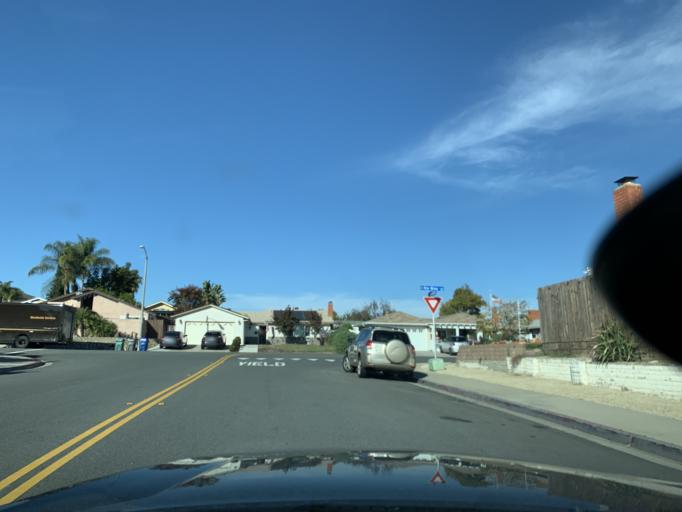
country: US
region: California
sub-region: San Diego County
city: Santee
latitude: 32.8553
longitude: -116.9807
